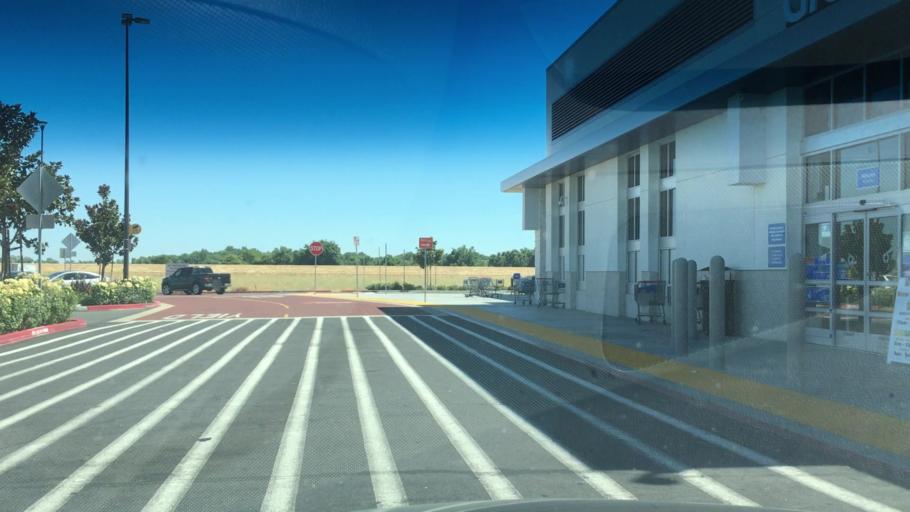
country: US
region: California
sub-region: Sacramento County
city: Parkway
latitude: 38.4595
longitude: -121.4921
